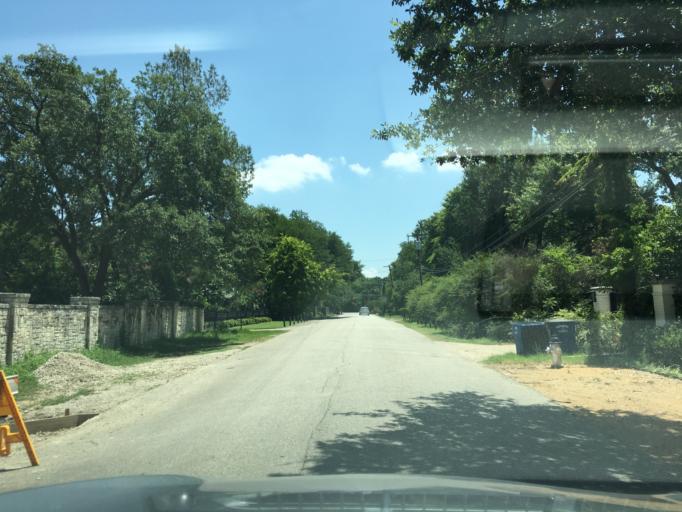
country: US
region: Texas
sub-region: Dallas County
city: University Park
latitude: 32.8739
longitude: -96.8067
